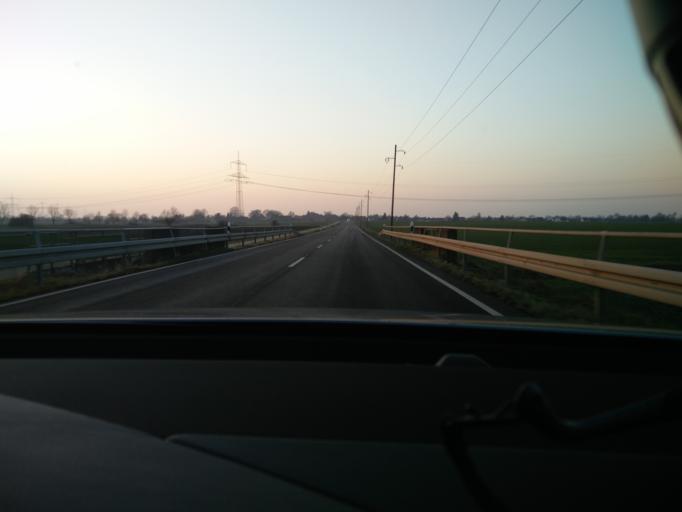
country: DE
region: Lower Saxony
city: Hohenhameln
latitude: 52.3059
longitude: 10.0642
